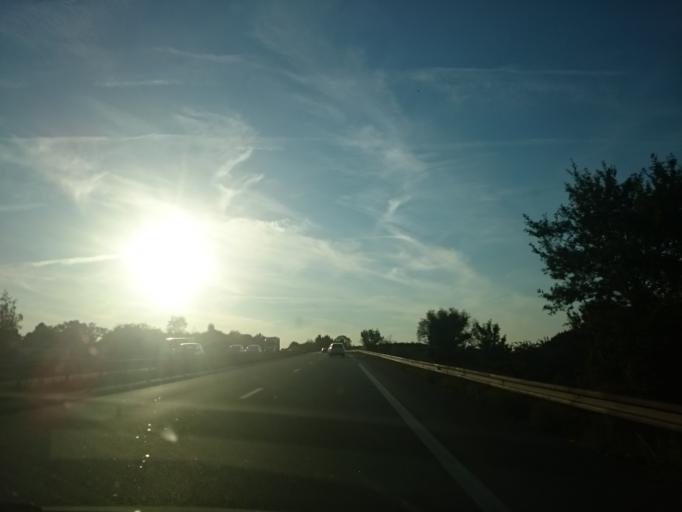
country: FR
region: Brittany
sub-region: Departement du Morbihan
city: Vannes
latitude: 47.6701
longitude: -2.7441
